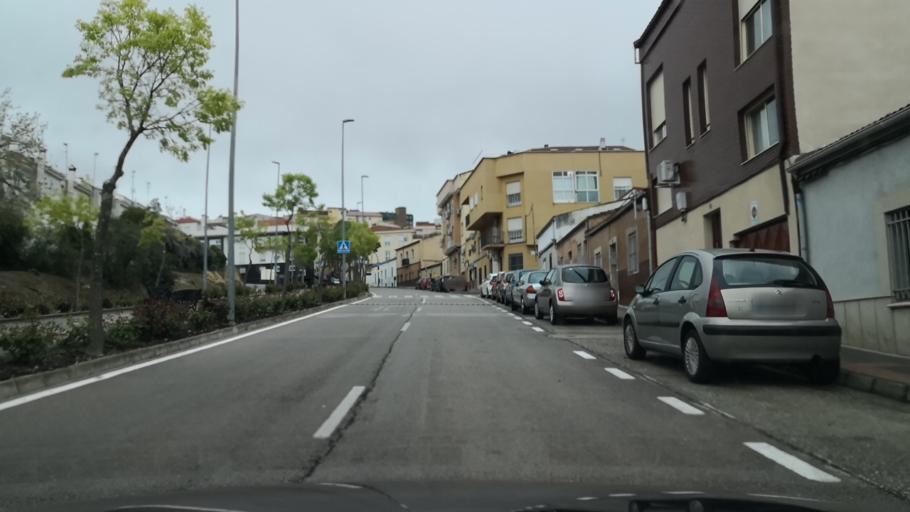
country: ES
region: Extremadura
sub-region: Provincia de Caceres
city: Caceres
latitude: 39.4811
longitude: -6.3794
